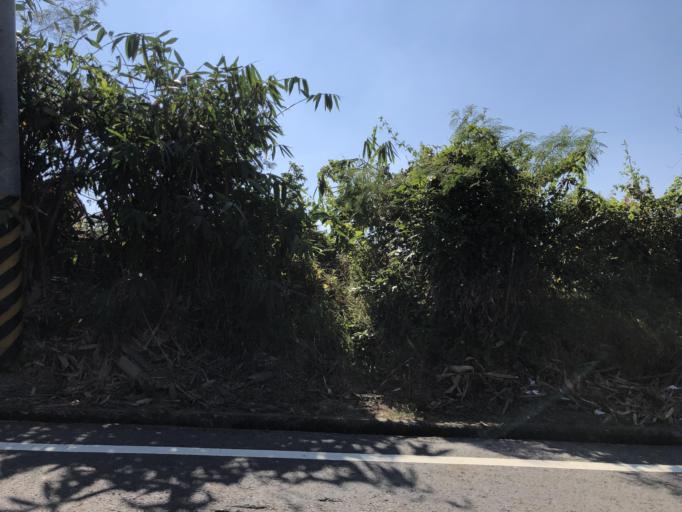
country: TW
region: Taiwan
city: Yujing
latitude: 23.0591
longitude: 120.3949
